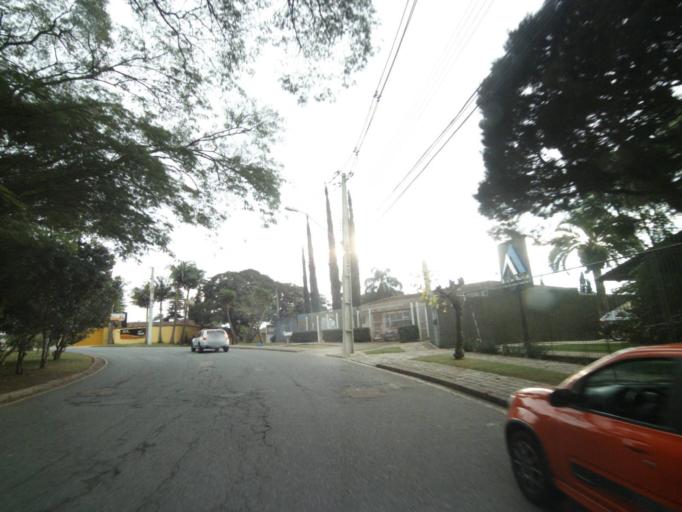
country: BR
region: Parana
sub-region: Curitiba
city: Curitiba
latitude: -25.3994
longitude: -49.2617
